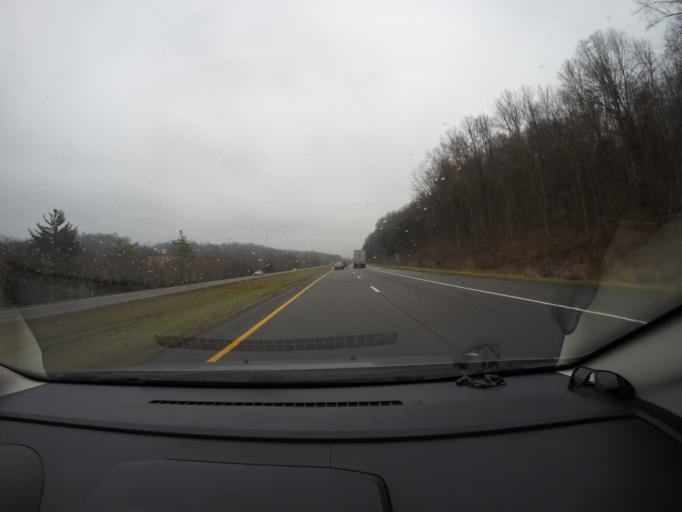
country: US
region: Tennessee
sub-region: Coffee County
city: New Union
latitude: 35.5625
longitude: -86.2106
